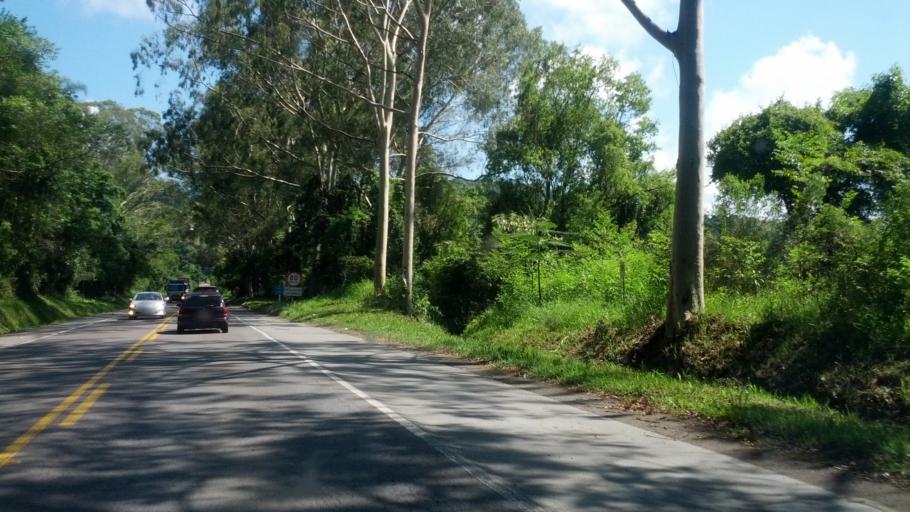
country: BR
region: Santa Catarina
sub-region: Ibirama
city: Ibirama
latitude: -27.1528
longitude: -49.5564
